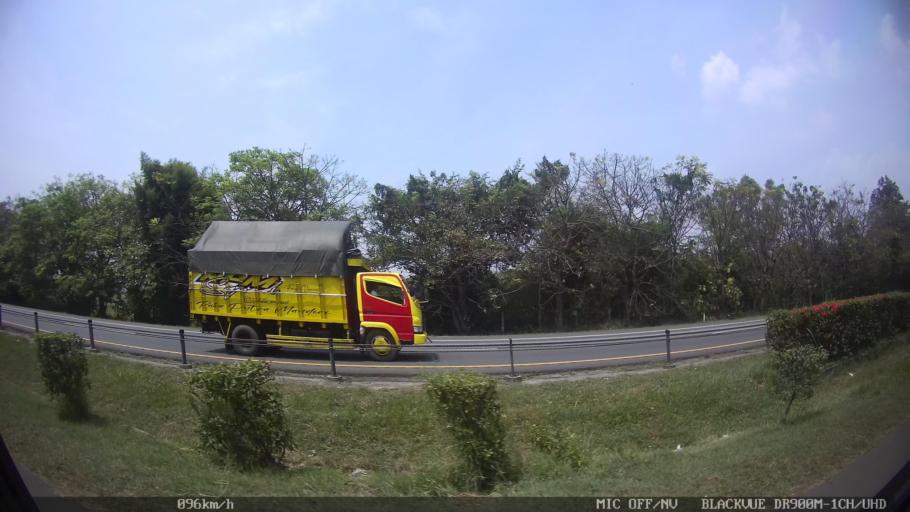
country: ID
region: Banten
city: Serang
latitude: -6.0688
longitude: 106.1272
